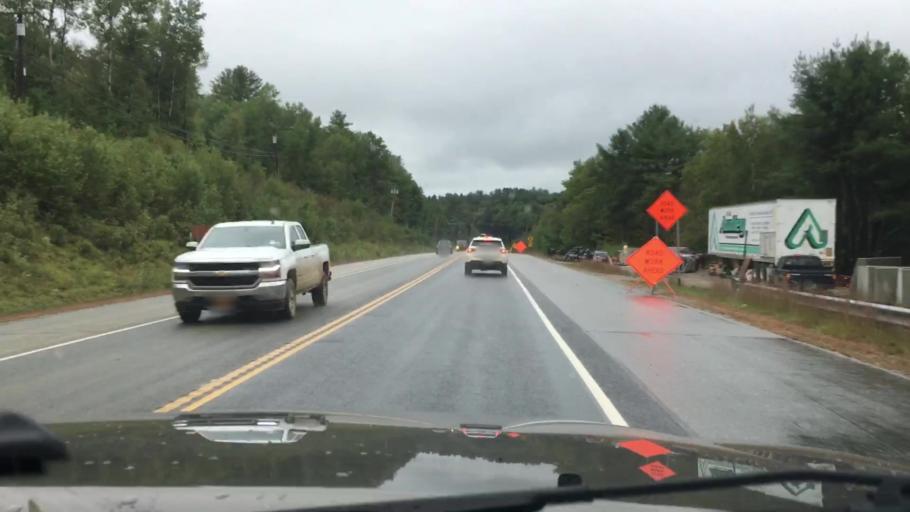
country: US
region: New Hampshire
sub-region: Cheshire County
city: Marlborough
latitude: 42.9954
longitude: -72.1912
